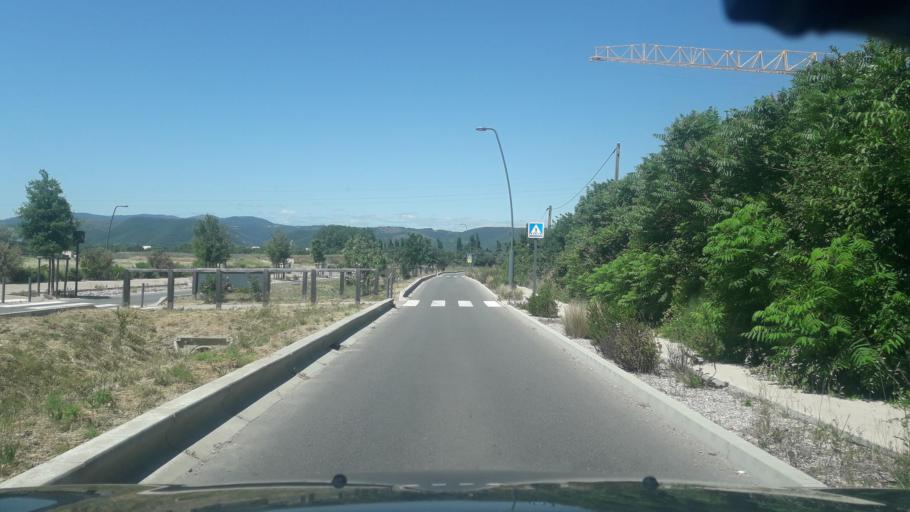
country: FR
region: Rhone-Alpes
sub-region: Departement de la Drome
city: Livron-sur-Drome
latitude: 44.7801
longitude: 4.8255
